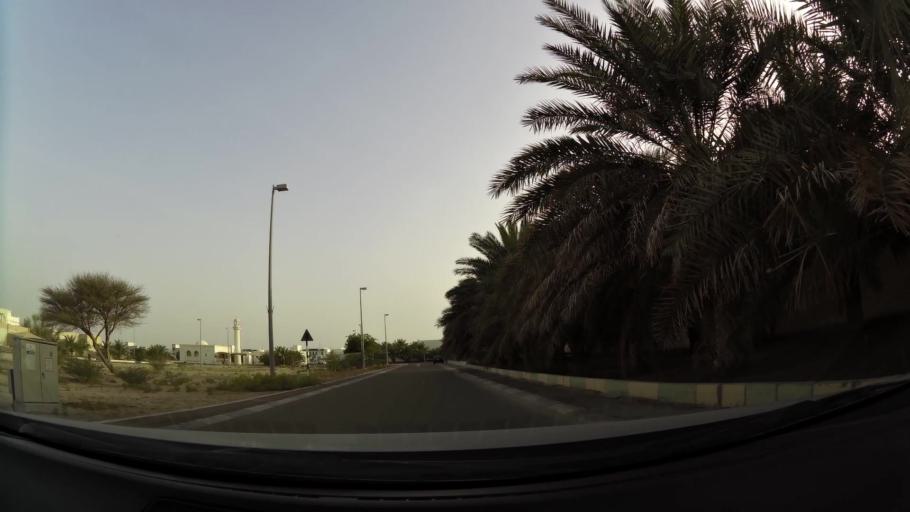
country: AE
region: Abu Dhabi
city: Al Ain
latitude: 24.1159
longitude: 55.7119
